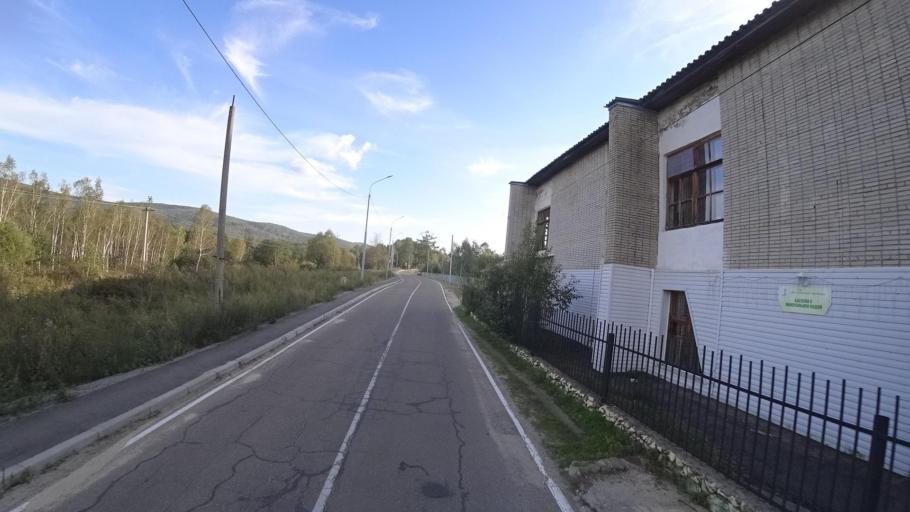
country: RU
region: Jewish Autonomous Oblast
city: Kul'dur
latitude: 49.2083
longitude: 131.6217
